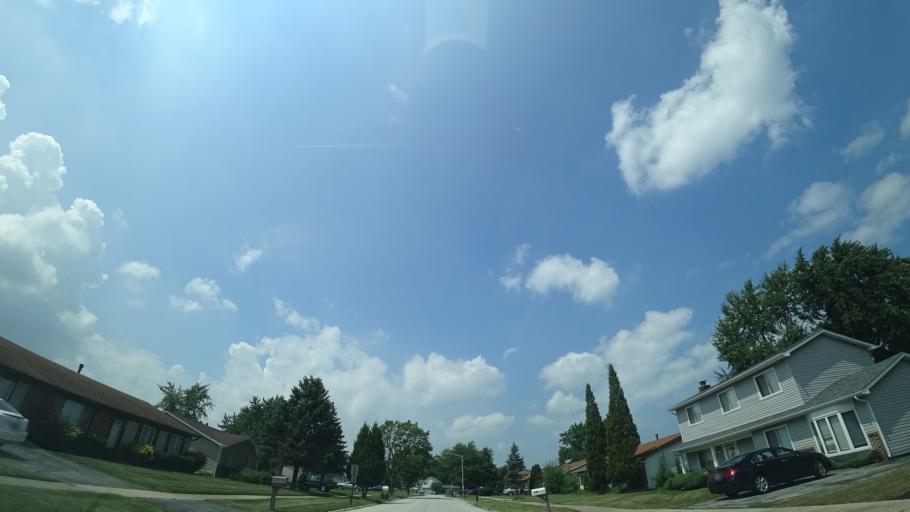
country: US
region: Illinois
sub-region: Will County
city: Frankfort Square
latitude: 41.5261
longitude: -87.7601
